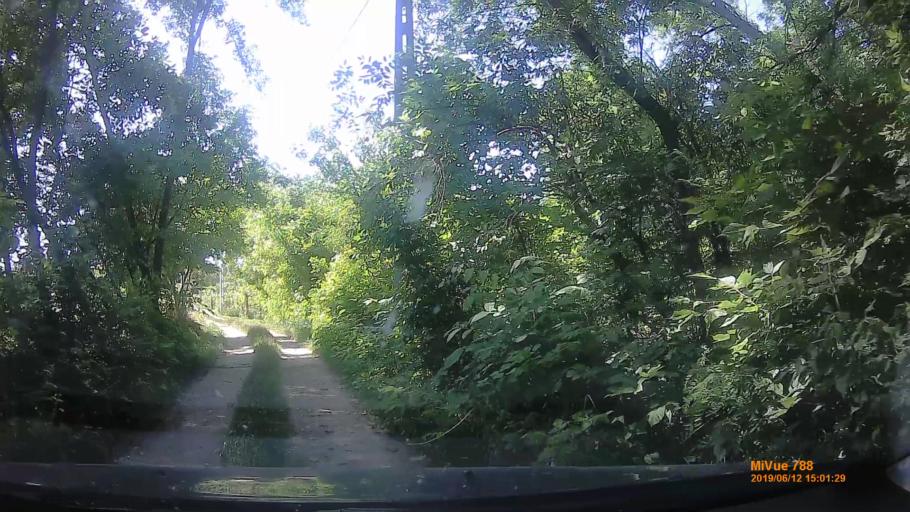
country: HU
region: Csongrad
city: Mako
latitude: 46.2063
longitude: 20.4631
